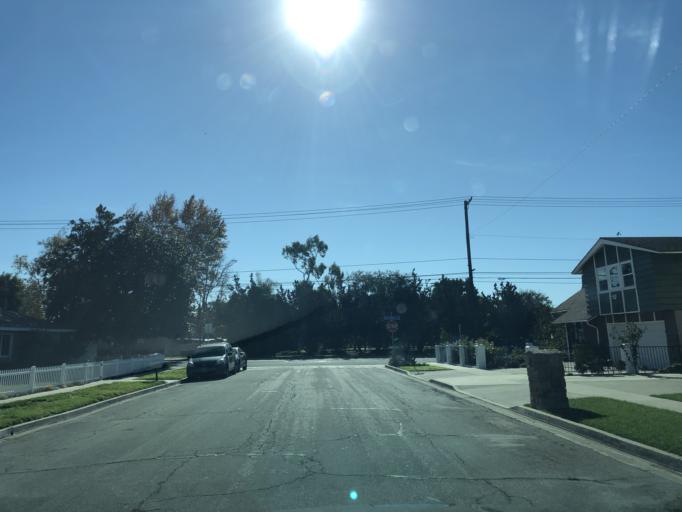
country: US
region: California
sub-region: Orange County
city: Orange
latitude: 33.7738
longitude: -117.8386
